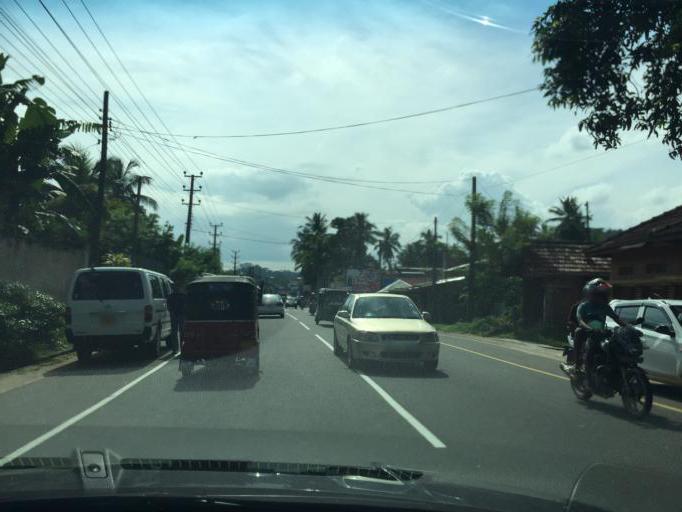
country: LK
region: Western
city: Horana South
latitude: 6.7204
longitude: 80.0728
